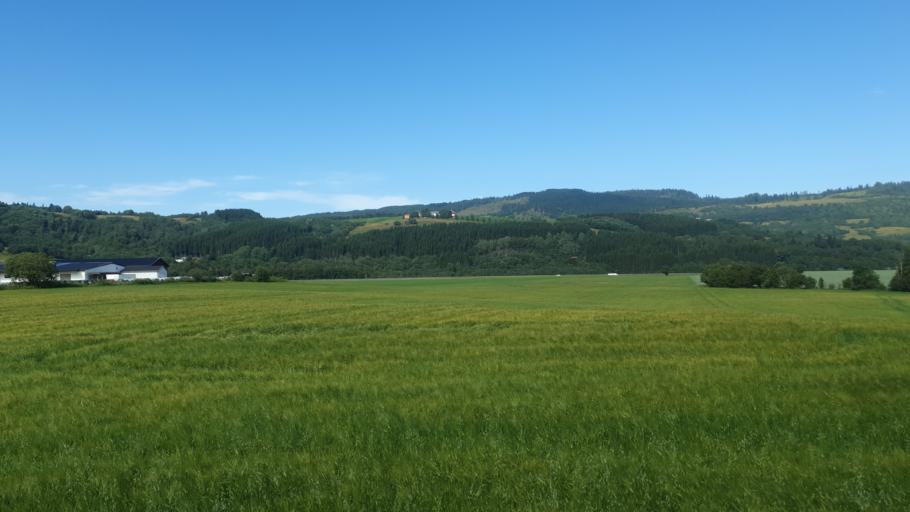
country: NO
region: Sor-Trondelag
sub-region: Orkdal
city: Orkanger
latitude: 63.2689
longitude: 9.8166
